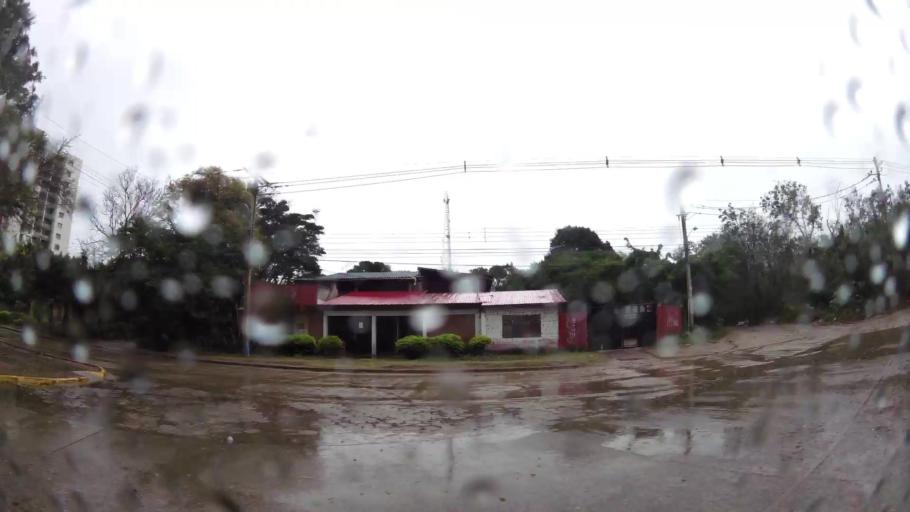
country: BO
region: Santa Cruz
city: Santa Cruz de la Sierra
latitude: -17.7862
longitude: -63.2237
